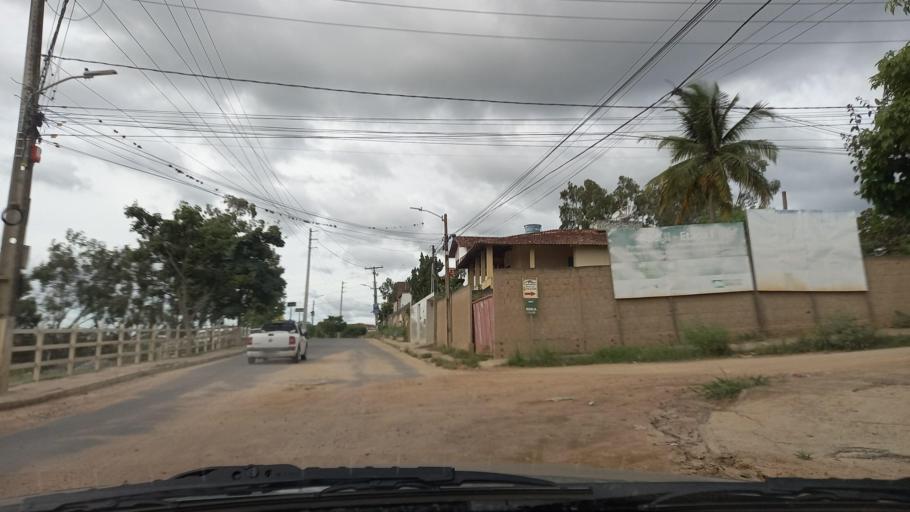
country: BR
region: Pernambuco
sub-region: Gravata
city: Gravata
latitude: -8.2053
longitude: -35.5545
